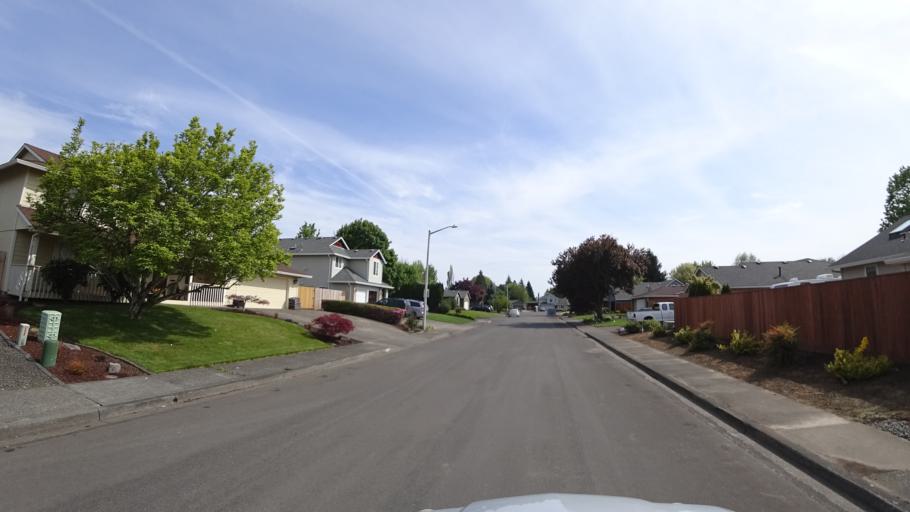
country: US
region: Oregon
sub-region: Washington County
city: Rockcreek
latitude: 45.5369
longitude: -122.9267
